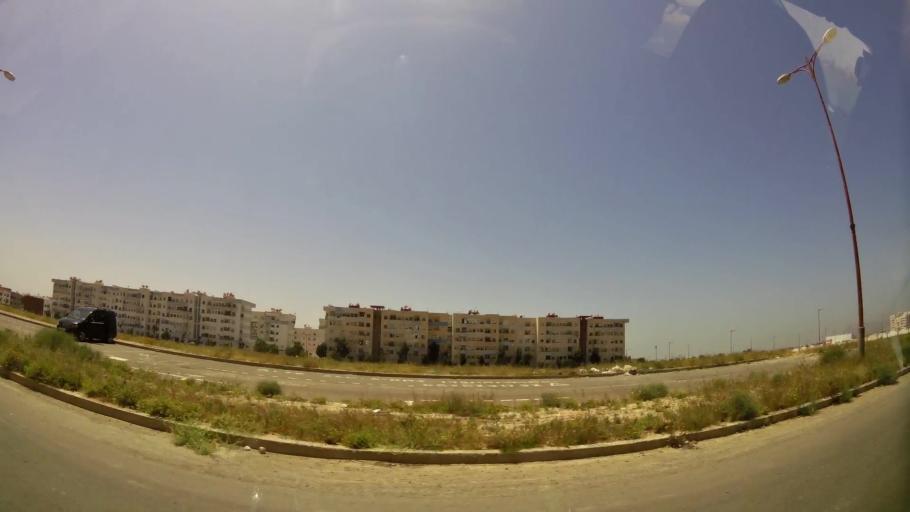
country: MA
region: Oued ed Dahab-Lagouira
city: Dakhla
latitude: 30.4335
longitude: -9.5639
